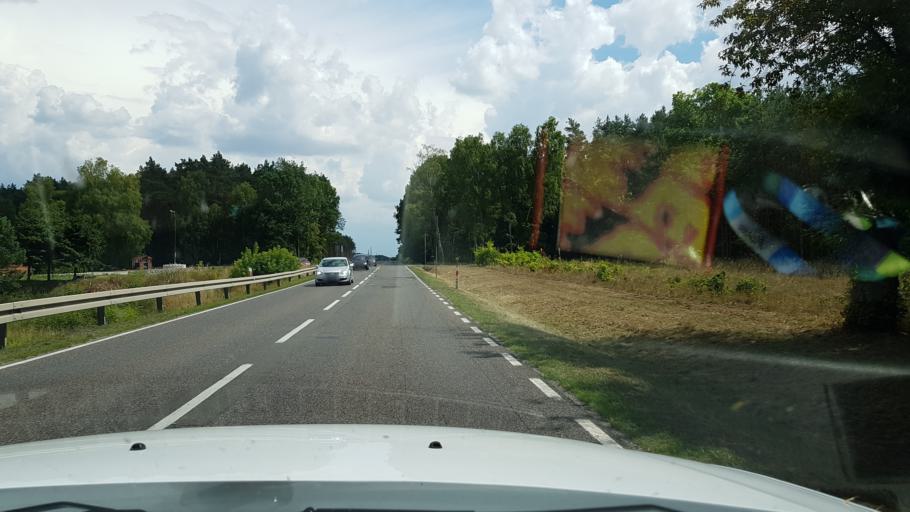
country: PL
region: West Pomeranian Voivodeship
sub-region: Powiat walecki
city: Walcz
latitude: 53.3022
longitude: 16.4097
